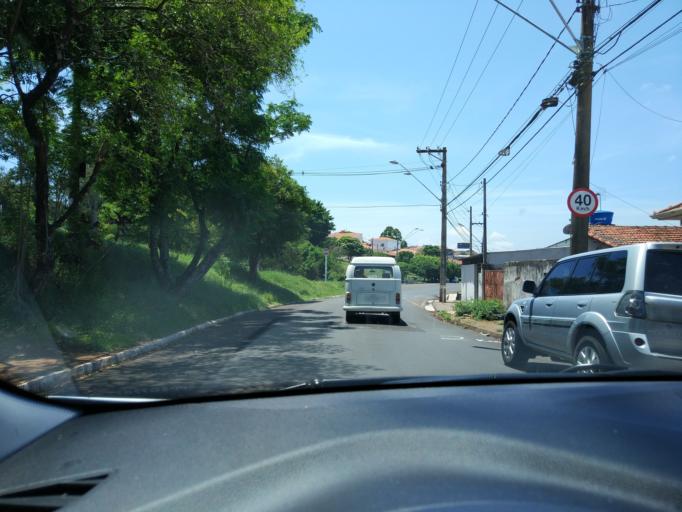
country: BR
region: Sao Paulo
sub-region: Botucatu
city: Botucatu
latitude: -22.8682
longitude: -48.4415
